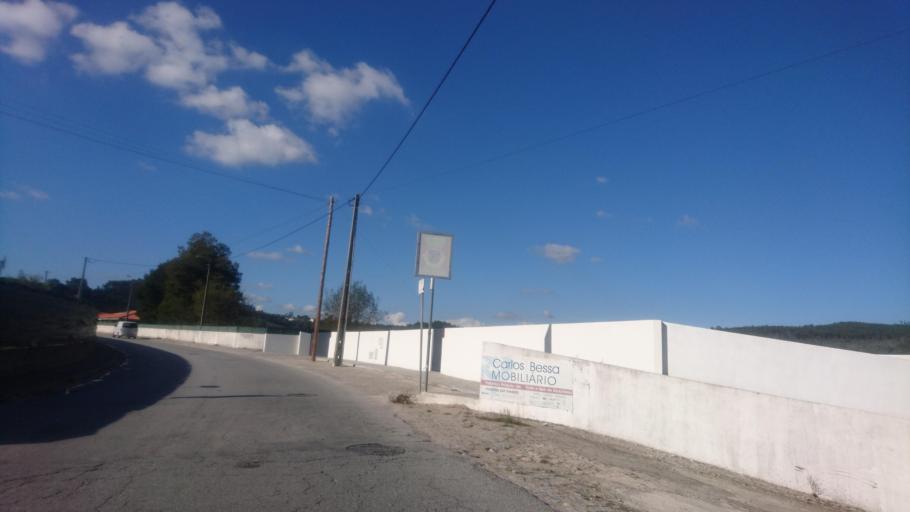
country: PT
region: Porto
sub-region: Paredes
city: Madalena
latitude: 41.2297
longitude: -8.3453
